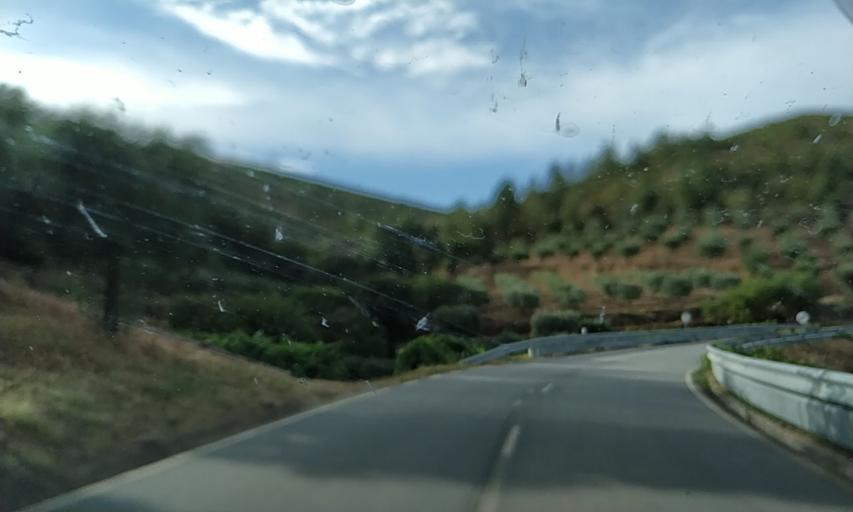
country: PT
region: Viseu
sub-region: Sao Joao da Pesqueira
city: Sao Joao da Pesqueira
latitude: 41.0999
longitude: -7.4622
